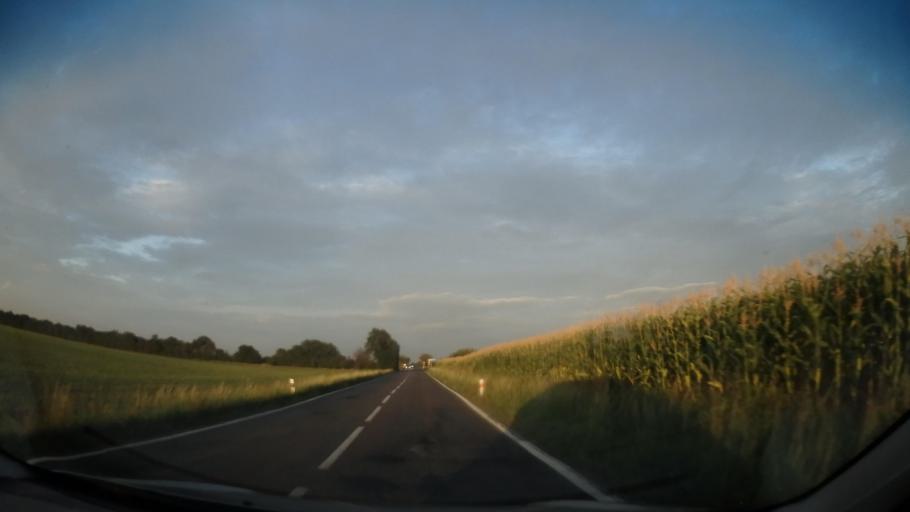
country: CZ
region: Central Bohemia
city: Milovice
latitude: 50.2261
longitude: 14.9221
